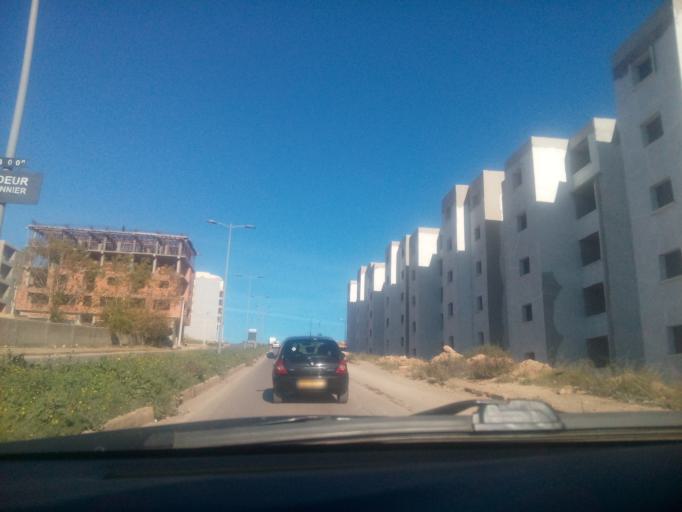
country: DZ
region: Oran
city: Bir el Djir
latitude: 35.7445
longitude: -0.5487
